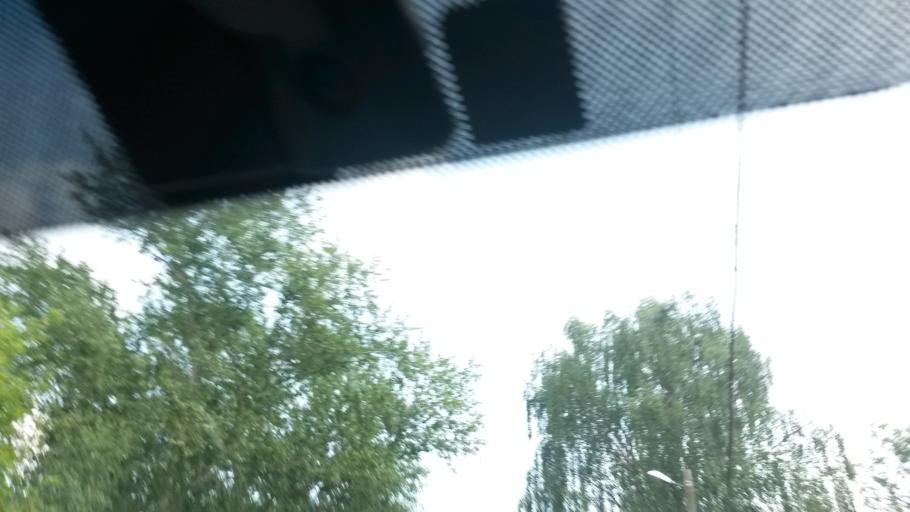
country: RU
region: Ivanovo
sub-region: Gorod Ivanovo
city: Ivanovo
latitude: 57.0066
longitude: 40.9599
